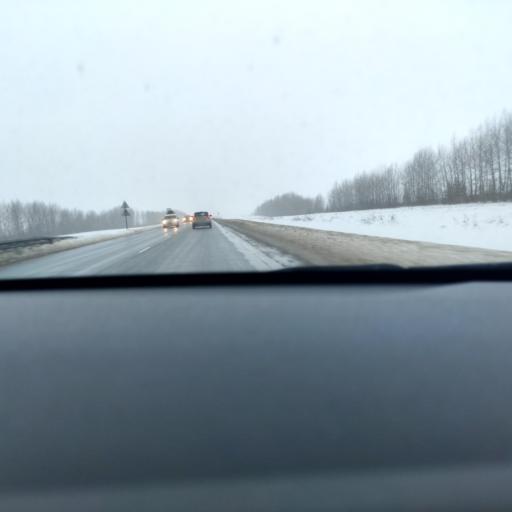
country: RU
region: Tatarstan
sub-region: Chistopol'skiy Rayon
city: Chistopol'
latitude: 55.3260
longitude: 50.4380
